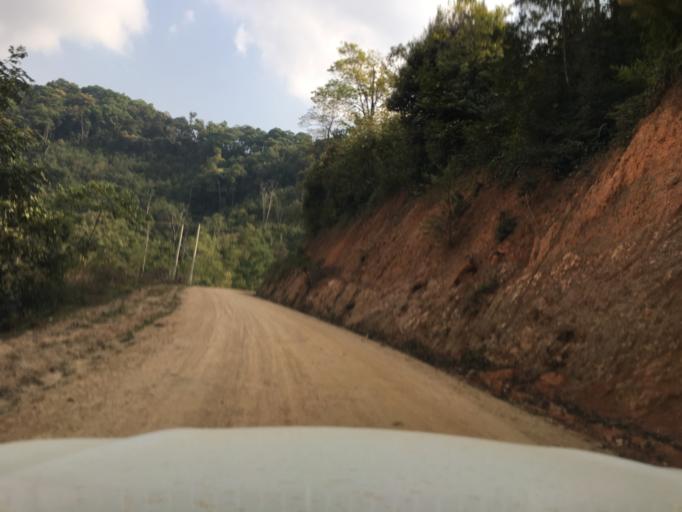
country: LA
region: Houaphan
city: Huameung
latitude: 20.2045
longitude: 103.8494
